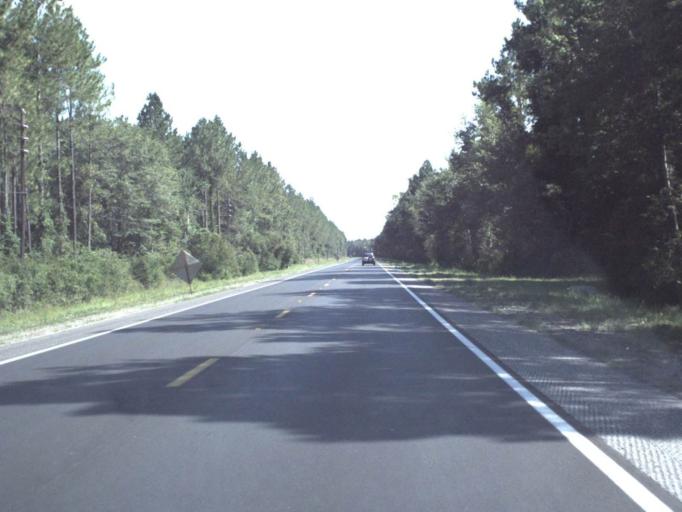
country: US
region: Florida
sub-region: Alachua County
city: Alachua
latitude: 29.7296
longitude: -82.3539
